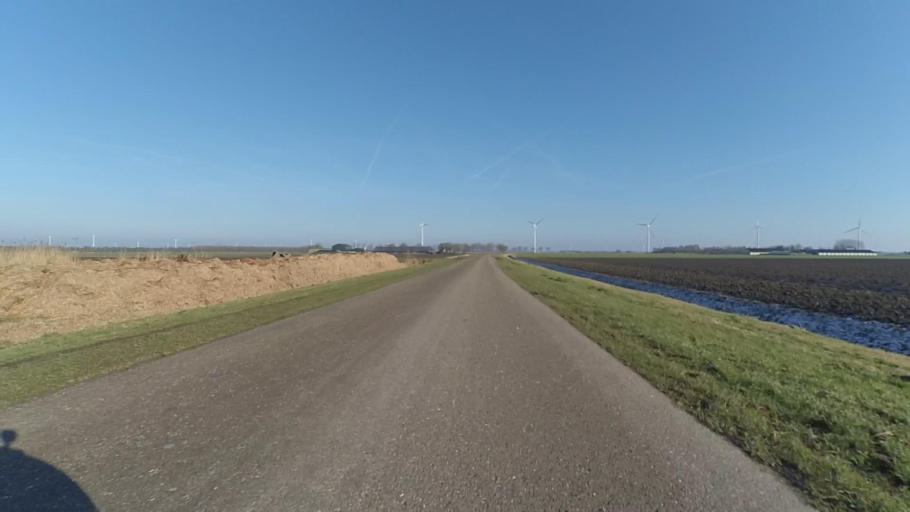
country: NL
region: Utrecht
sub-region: Gemeente Bunschoten
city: Spakenburg
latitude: 52.3041
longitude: 5.3663
